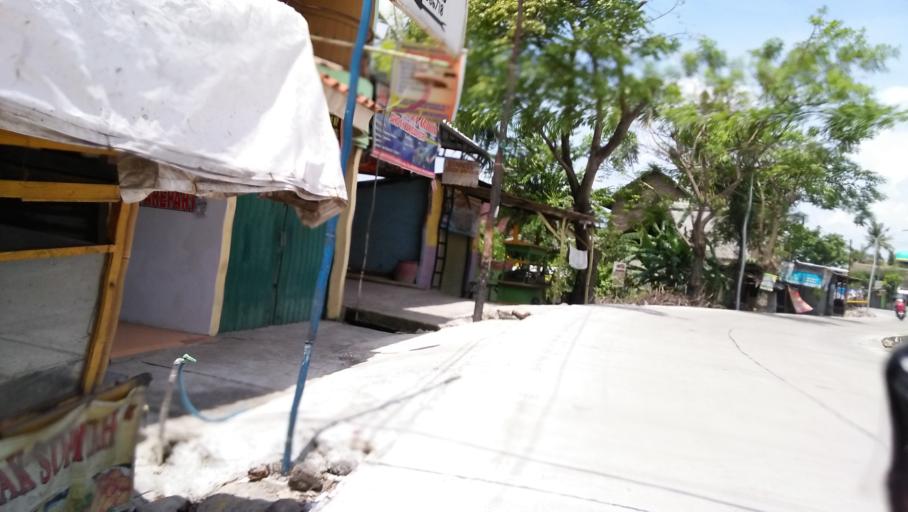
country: ID
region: Central Java
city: Mranggen
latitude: -6.9800
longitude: 110.4801
